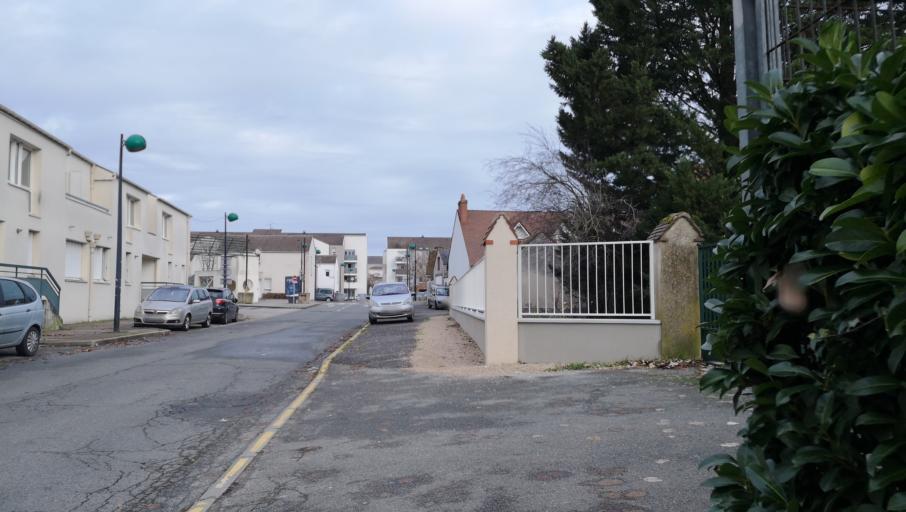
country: FR
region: Centre
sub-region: Departement du Loiret
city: Saint-Jean-de-Braye
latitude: 47.9112
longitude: 1.9672
